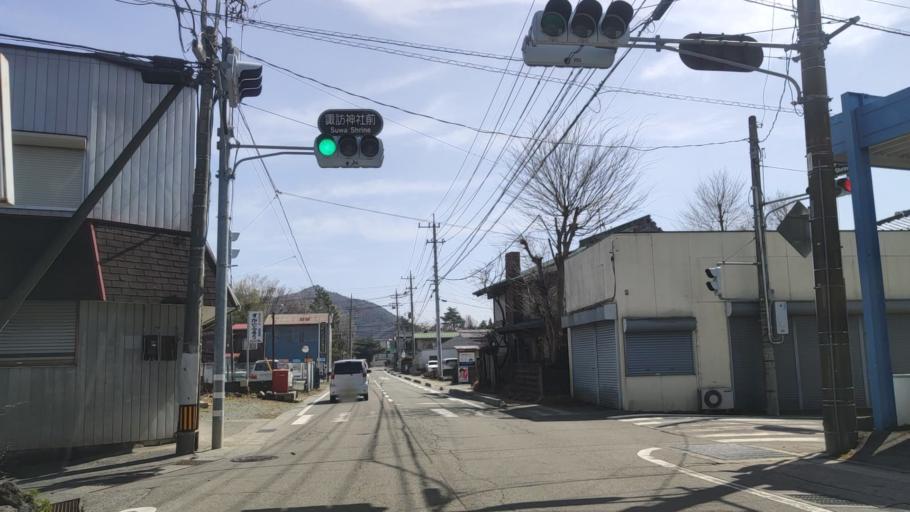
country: JP
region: Yamanashi
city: Fujikawaguchiko
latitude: 35.5068
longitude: 138.7489
